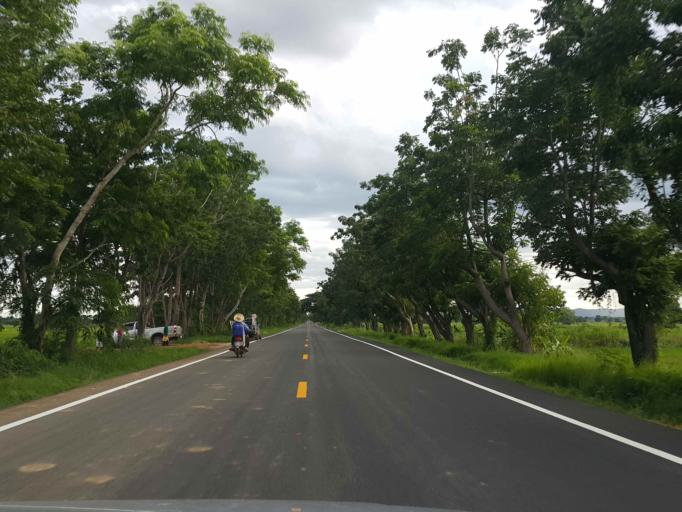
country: TH
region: Sukhothai
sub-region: Amphoe Si Satchanalai
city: Si Satchanalai
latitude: 17.4944
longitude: 99.7506
